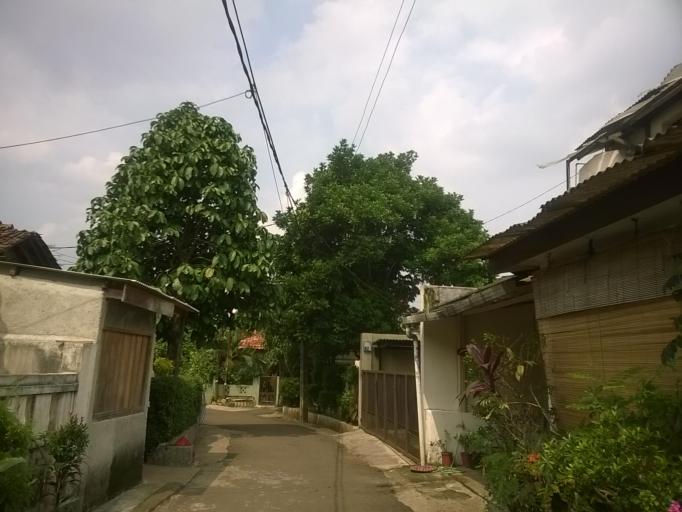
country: ID
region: West Java
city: Pamulang
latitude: -6.3142
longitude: 106.7790
